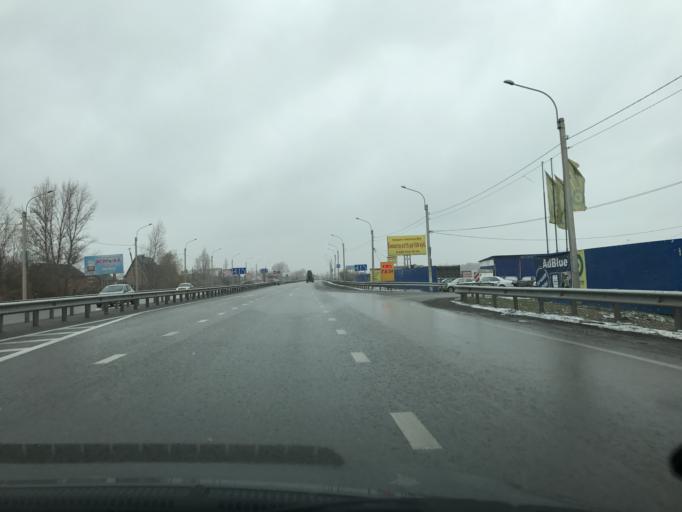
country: RU
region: Rostov
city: Bataysk
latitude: 47.1536
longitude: 39.7707
